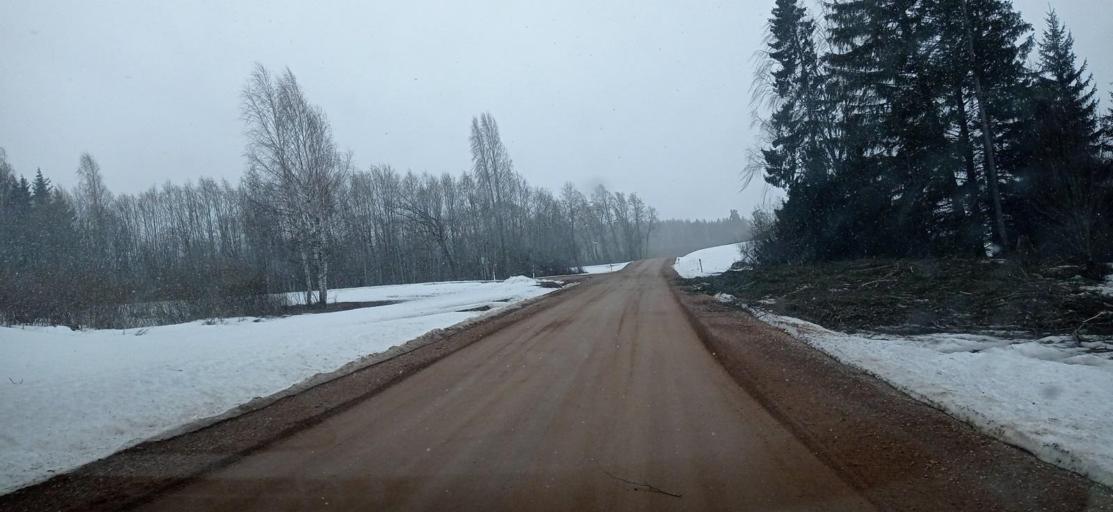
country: EE
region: Tartu
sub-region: UElenurme vald
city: Ulenurme
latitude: 58.1131
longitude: 26.6989
